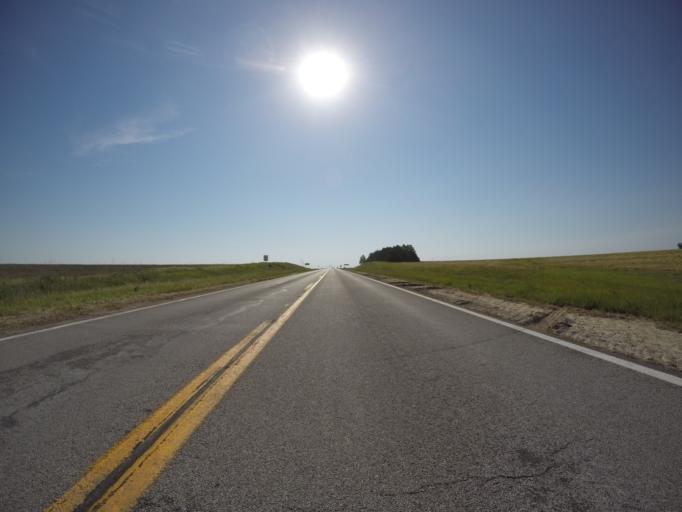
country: US
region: Nebraska
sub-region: Pawnee County
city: Pawnee City
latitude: 40.0446
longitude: -96.3539
